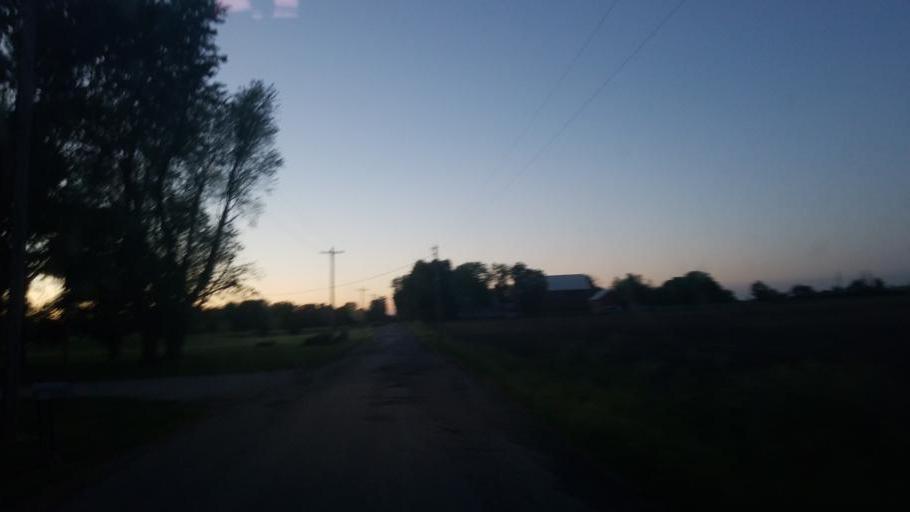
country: US
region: Indiana
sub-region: Marshall County
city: Bremen
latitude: 41.4574
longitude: -86.1176
